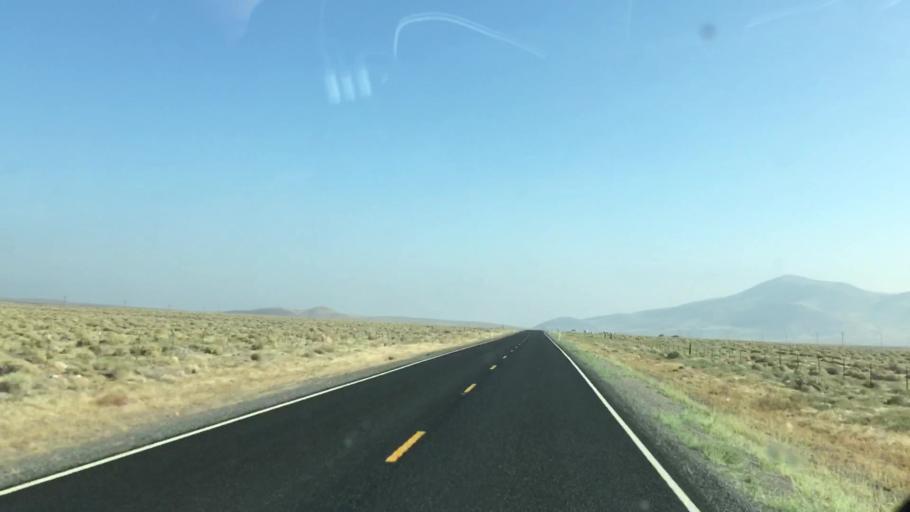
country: US
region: Nevada
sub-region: Lyon County
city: Fernley
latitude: 39.7190
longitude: -119.3345
